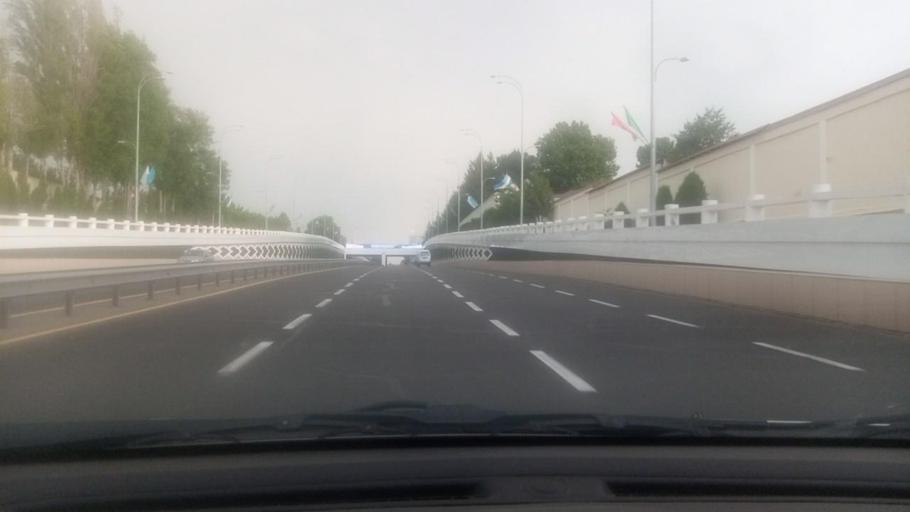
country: UZ
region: Toshkent
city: Salor
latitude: 41.3304
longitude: 69.3526
